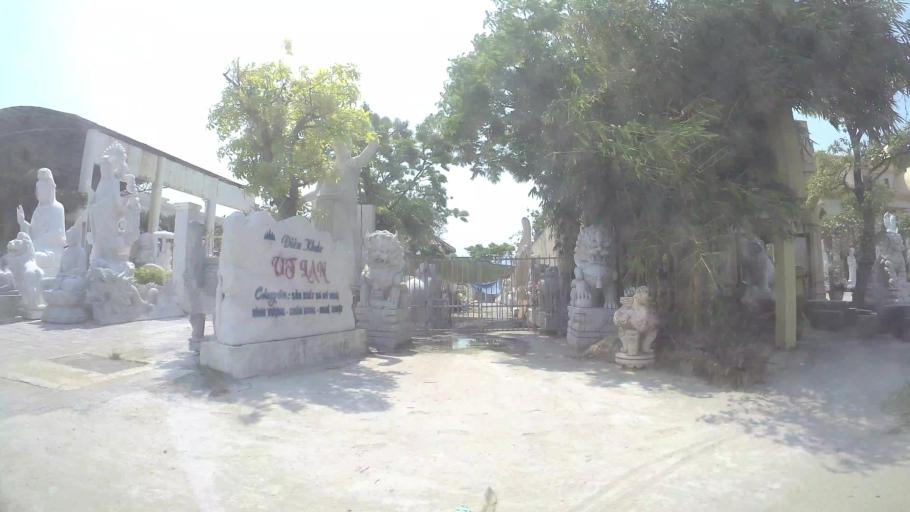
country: VN
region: Da Nang
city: Ngu Hanh Son
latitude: 16.0030
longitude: 108.2667
